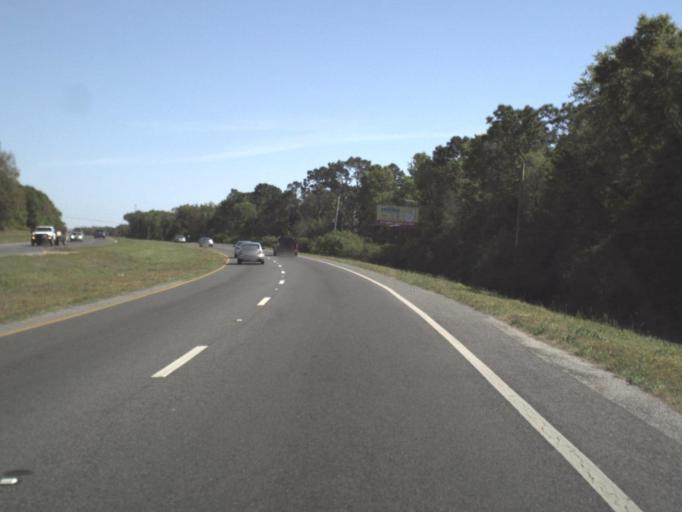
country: US
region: Florida
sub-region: Escambia County
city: Bellview
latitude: 30.4569
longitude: -87.2990
